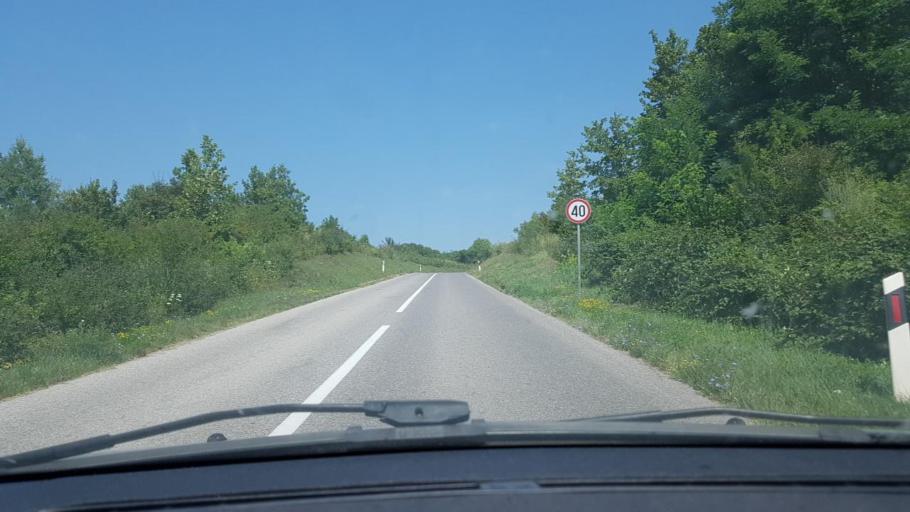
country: BA
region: Federation of Bosnia and Herzegovina
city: Velika Kladusa
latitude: 45.2049
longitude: 15.7732
